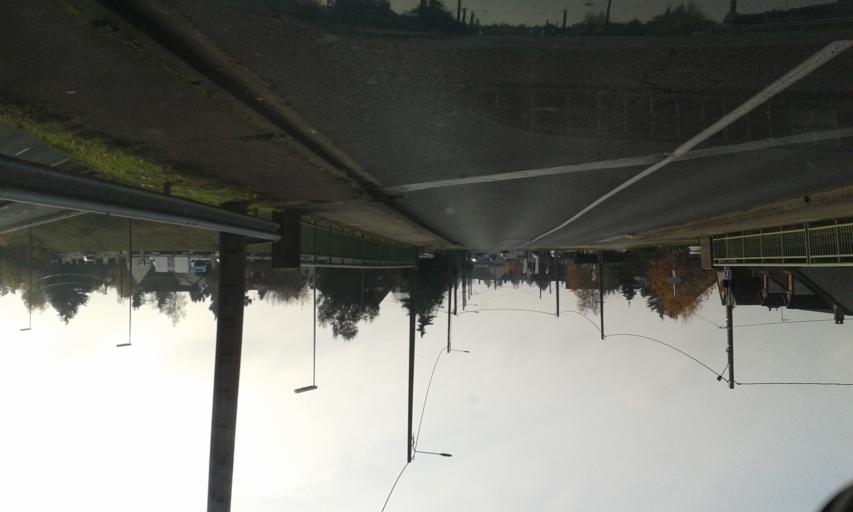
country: FR
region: Centre
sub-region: Departement du Loiret
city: Olivet
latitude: 47.8592
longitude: 1.9122
